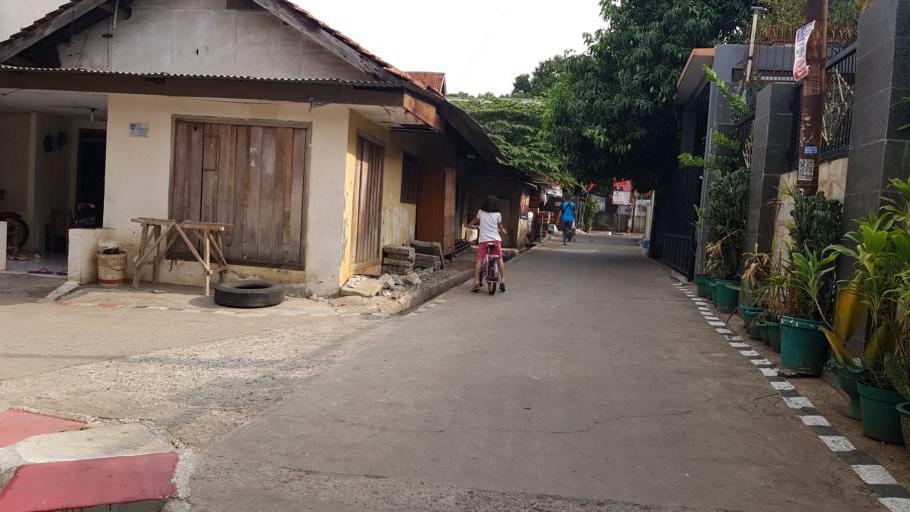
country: ID
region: West Java
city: Pamulang
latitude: -6.3264
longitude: 106.7982
